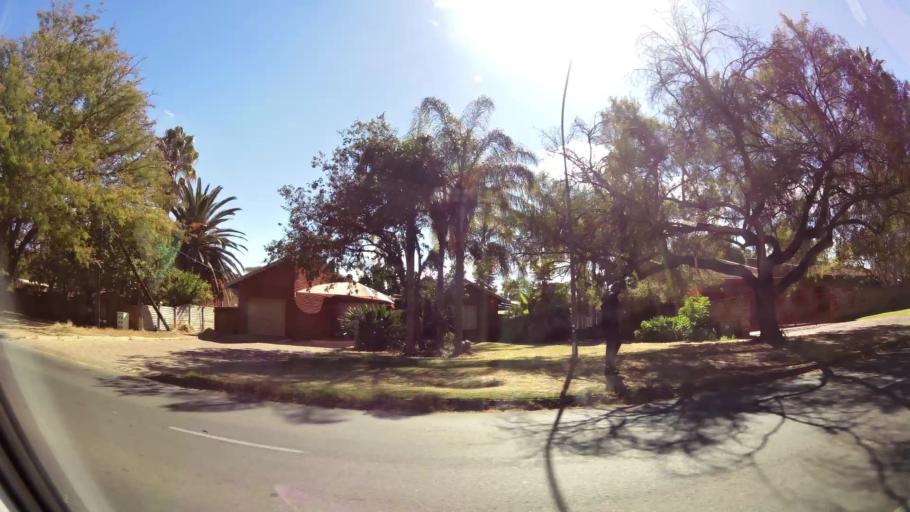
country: ZA
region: Limpopo
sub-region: Capricorn District Municipality
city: Polokwane
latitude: -23.9086
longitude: 29.4889
